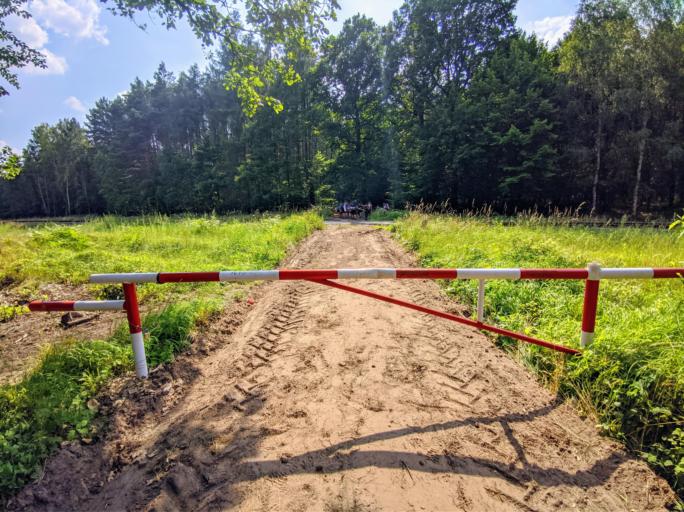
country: PL
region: Lubusz
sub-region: Powiat miedzyrzecki
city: Miedzyrzecz
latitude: 52.4994
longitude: 15.5313
